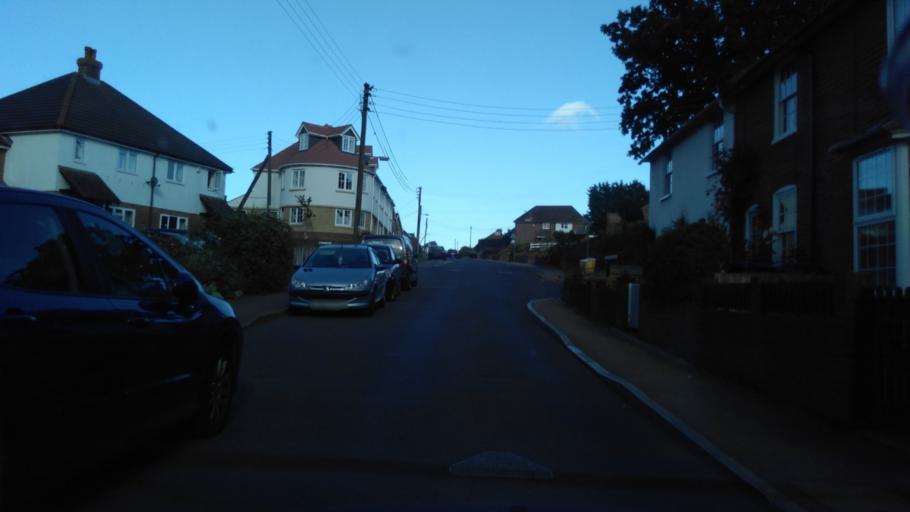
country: GB
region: England
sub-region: Kent
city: Chartham
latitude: 51.2530
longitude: 1.0050
